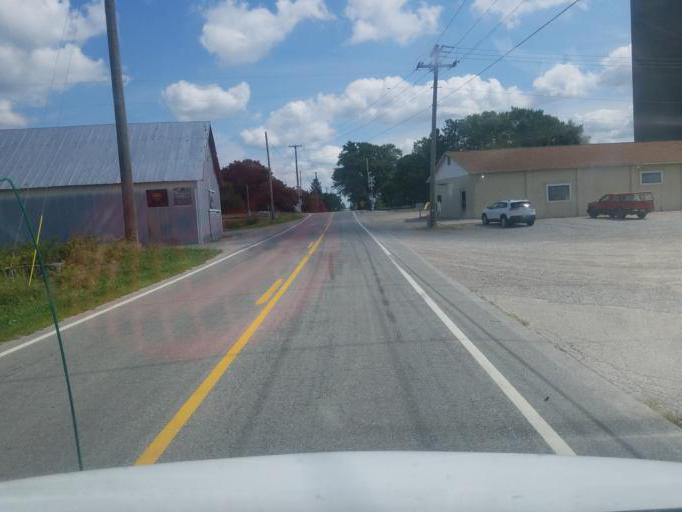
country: US
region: Ohio
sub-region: Marion County
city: Prospect
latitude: 40.3857
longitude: -83.1357
